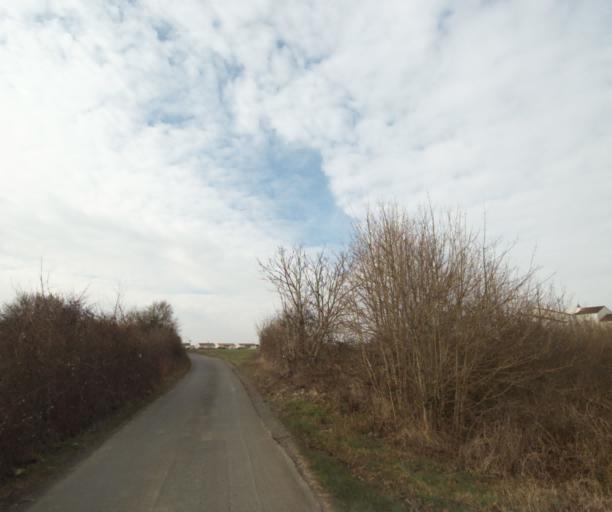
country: FR
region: Poitou-Charentes
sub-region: Departement des Deux-Sevres
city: Aiffres
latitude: 46.3126
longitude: -0.4308
